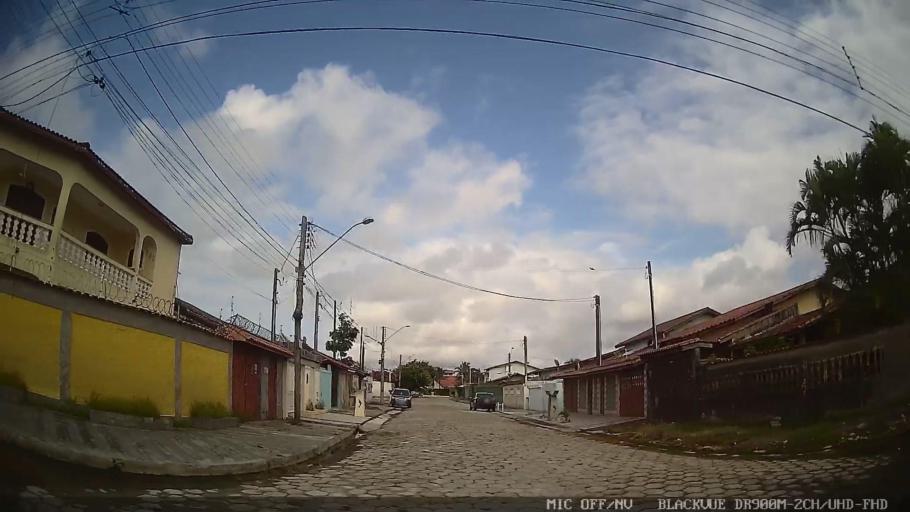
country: BR
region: Sao Paulo
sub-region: Itanhaem
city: Itanhaem
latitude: -24.1995
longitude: -46.8249
